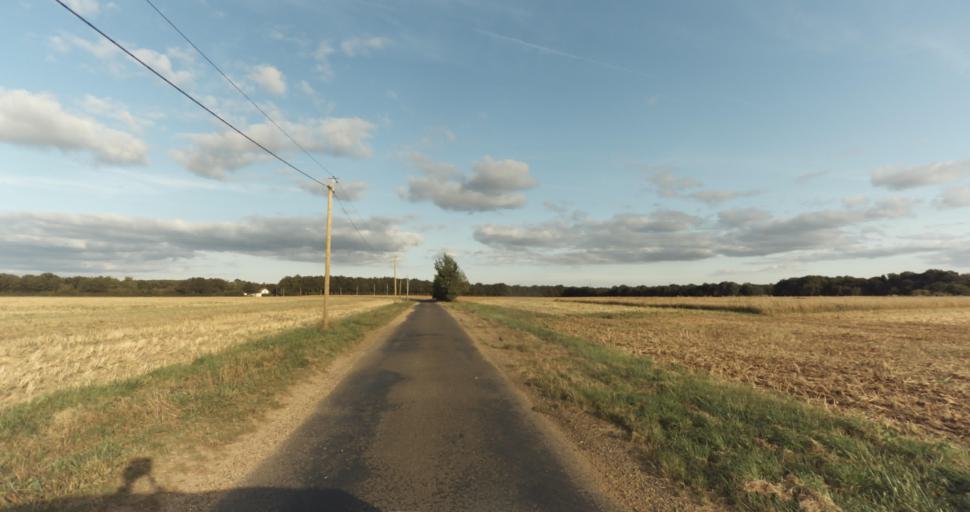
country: FR
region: Haute-Normandie
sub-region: Departement de l'Eure
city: Marcilly-sur-Eure
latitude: 48.8816
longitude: 1.2734
